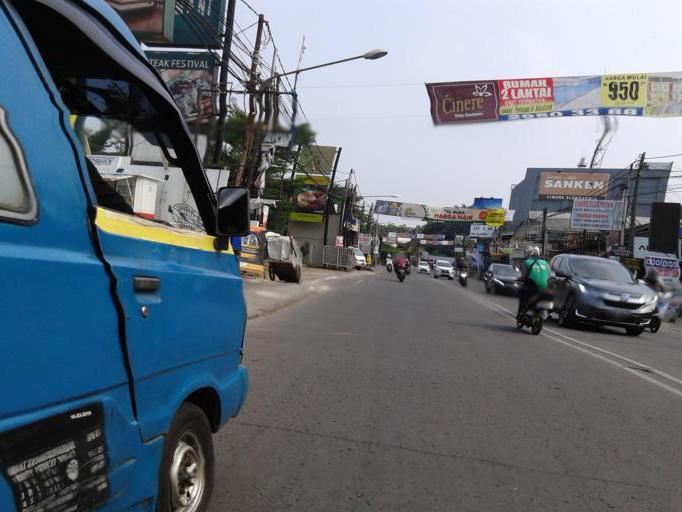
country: ID
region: West Java
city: Pamulang
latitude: -6.3269
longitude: 106.7850
